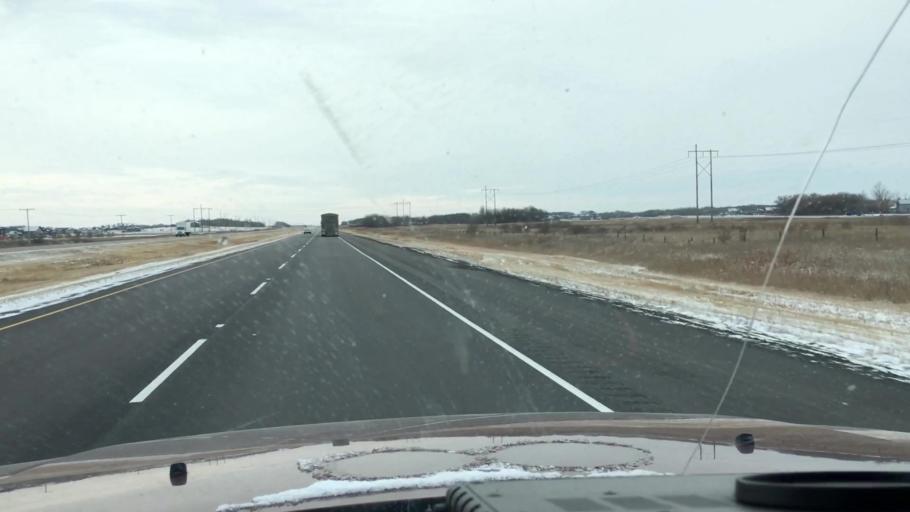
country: CA
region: Saskatchewan
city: Saskatoon
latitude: 51.9533
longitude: -106.5462
